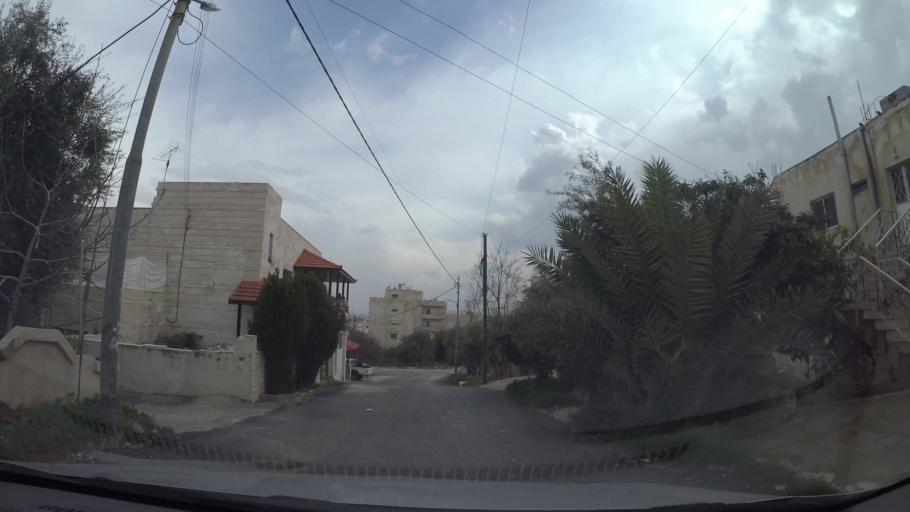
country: JO
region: Amman
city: Umm as Summaq
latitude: 31.8876
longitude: 35.8637
